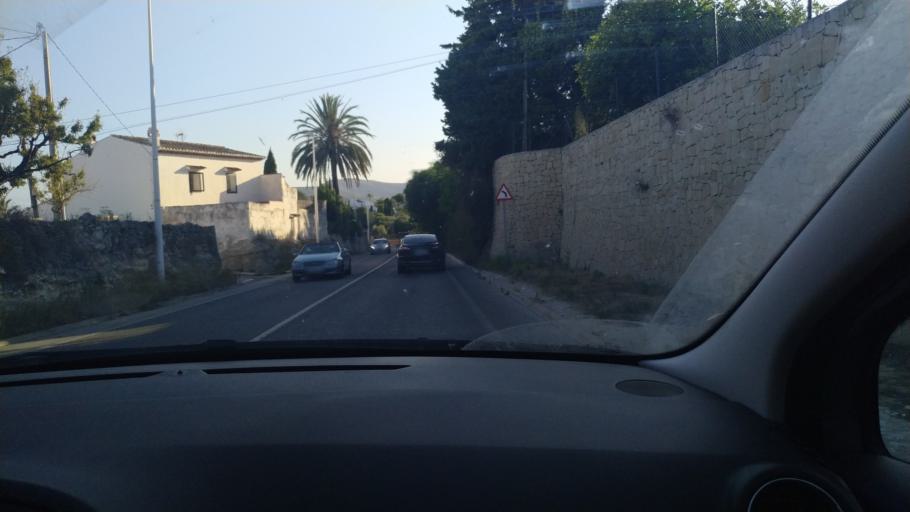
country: ES
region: Valencia
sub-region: Provincia de Alicante
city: Javea
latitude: 38.7843
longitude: 0.1583
